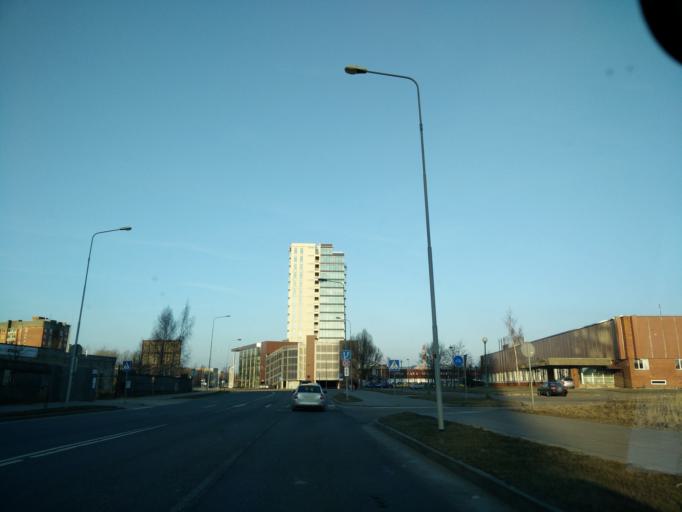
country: LT
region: Klaipedos apskritis
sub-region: Klaipeda
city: Klaipeda
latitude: 55.6913
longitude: 21.1487
